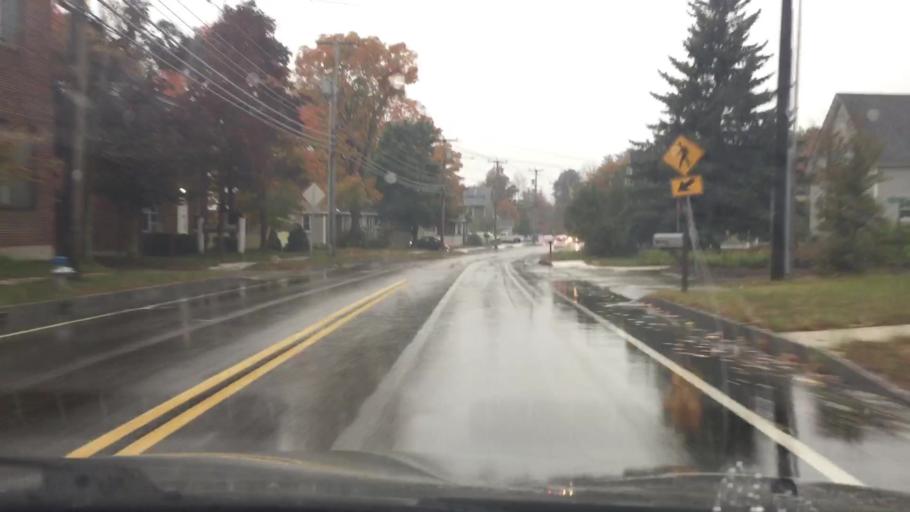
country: US
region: New Hampshire
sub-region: Cheshire County
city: Keene
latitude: 42.9495
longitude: -72.2703
